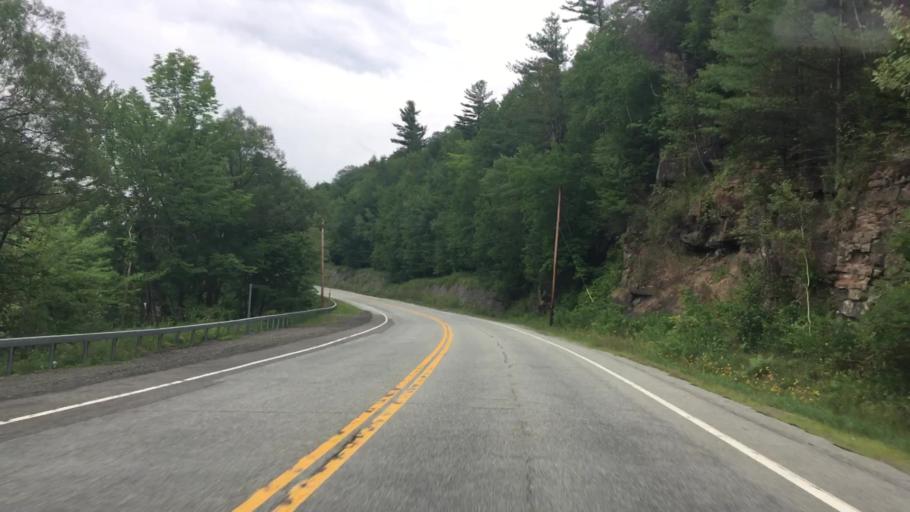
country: US
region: New York
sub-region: Essex County
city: Lake Placid
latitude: 44.2820
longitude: -73.7880
